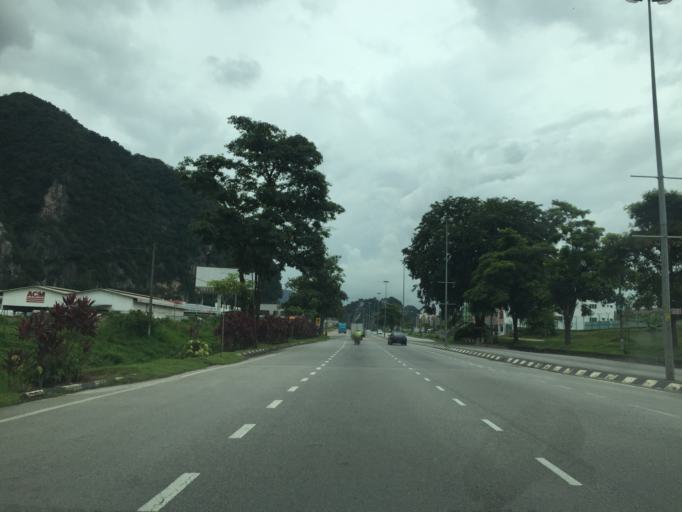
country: MY
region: Perak
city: Ipoh
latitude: 4.5577
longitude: 101.1132
